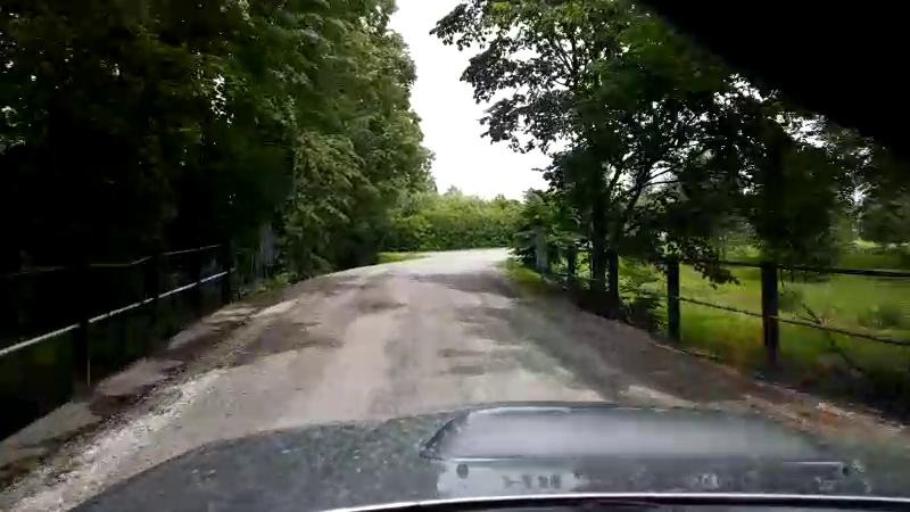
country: EE
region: Paernumaa
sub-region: Tootsi vald
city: Tootsi
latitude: 58.5388
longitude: 24.7346
